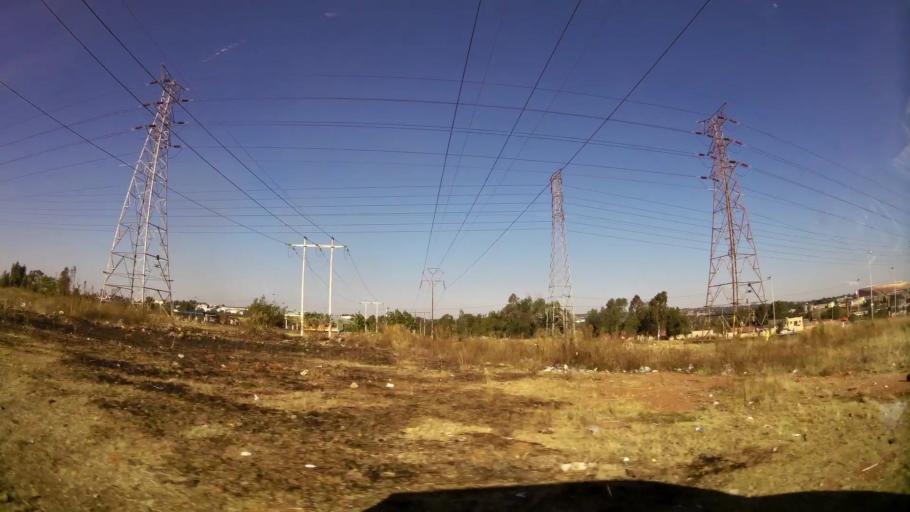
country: ZA
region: Gauteng
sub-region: City of Johannesburg Metropolitan Municipality
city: Johannesburg
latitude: -26.2156
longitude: 27.9832
